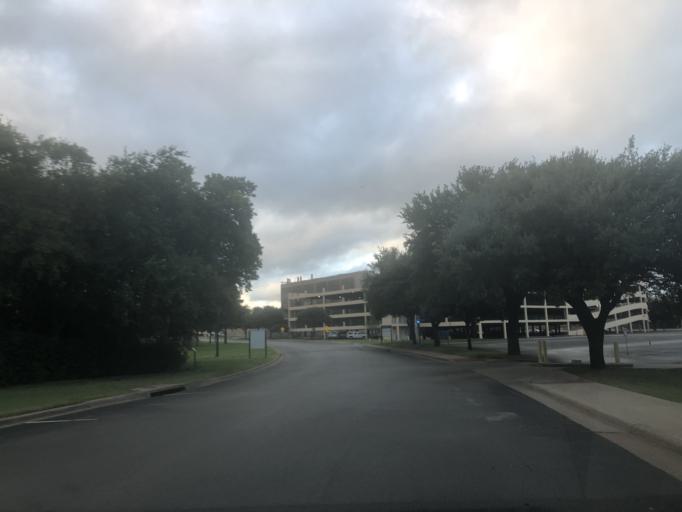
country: US
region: Texas
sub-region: Dallas County
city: Dallas
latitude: 32.8134
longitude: -96.8448
